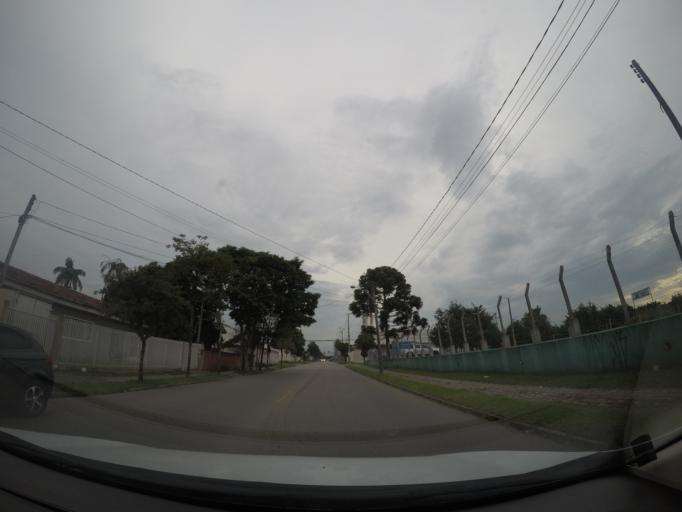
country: BR
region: Parana
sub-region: Curitiba
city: Curitiba
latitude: -25.4717
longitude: -49.2486
